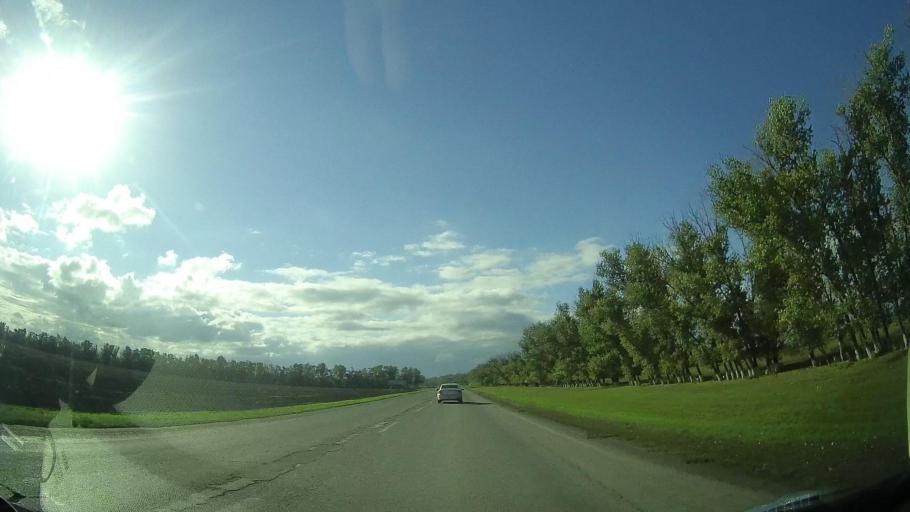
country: RU
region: Rostov
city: Tselina
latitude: 46.5327
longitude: 40.9952
